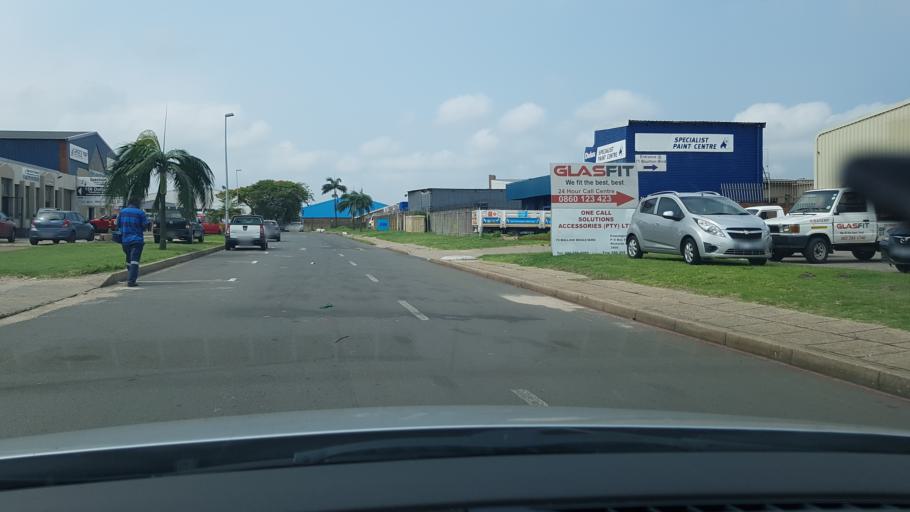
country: ZA
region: KwaZulu-Natal
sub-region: uThungulu District Municipality
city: Richards Bay
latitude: -28.7525
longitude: 32.0462
